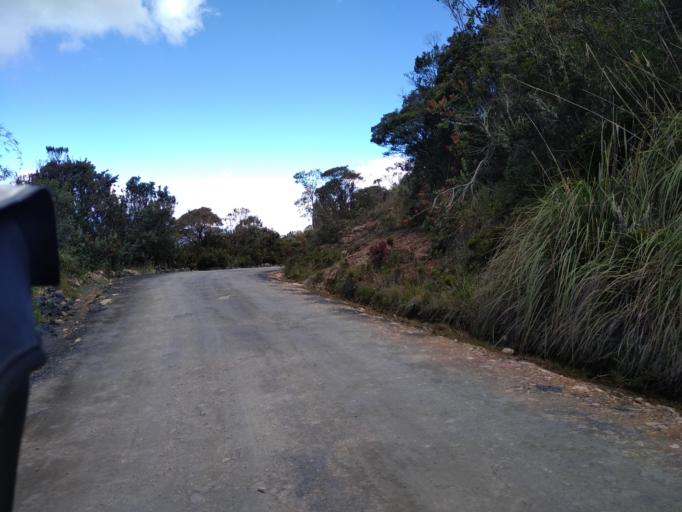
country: CO
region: Boyaca
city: Duitama
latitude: 5.9377
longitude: -73.0992
